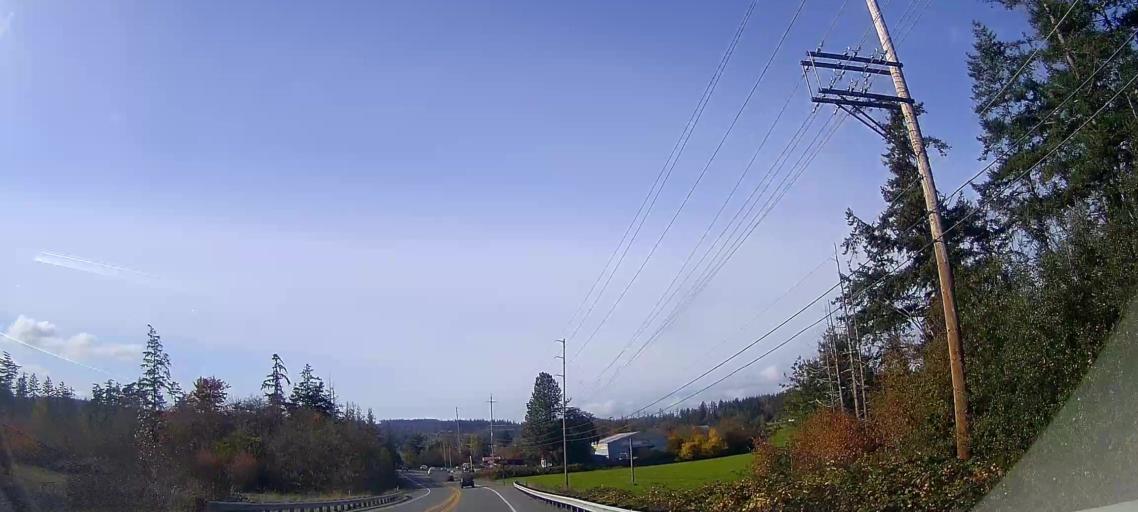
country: US
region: Washington
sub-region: Snohomish County
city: Stanwood
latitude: 48.2400
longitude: -122.4305
